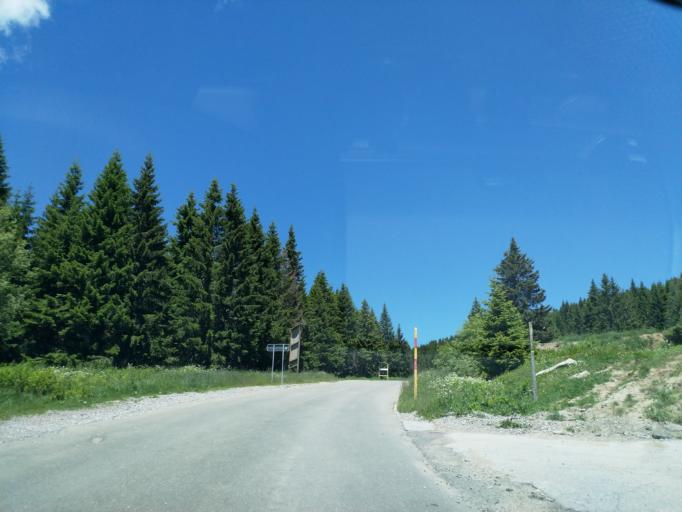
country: XK
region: Mitrovica
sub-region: Komuna e Leposaviqit
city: Leposaviq
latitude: 43.2927
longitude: 20.8163
